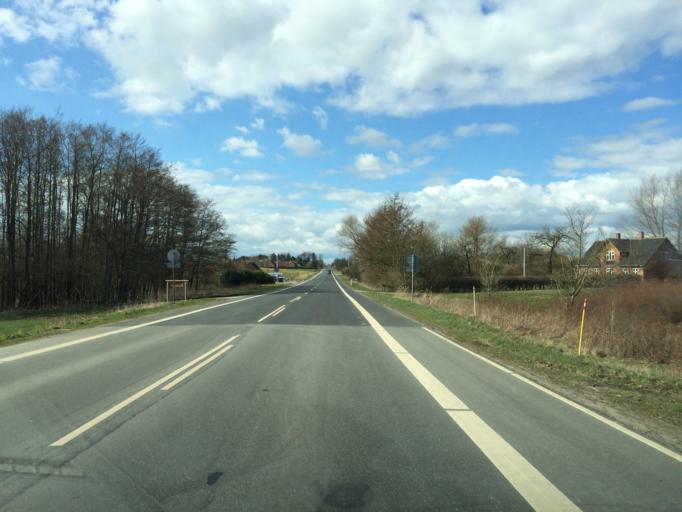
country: DK
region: South Denmark
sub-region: Assens Kommune
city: Arup
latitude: 55.4179
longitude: 10.0454
